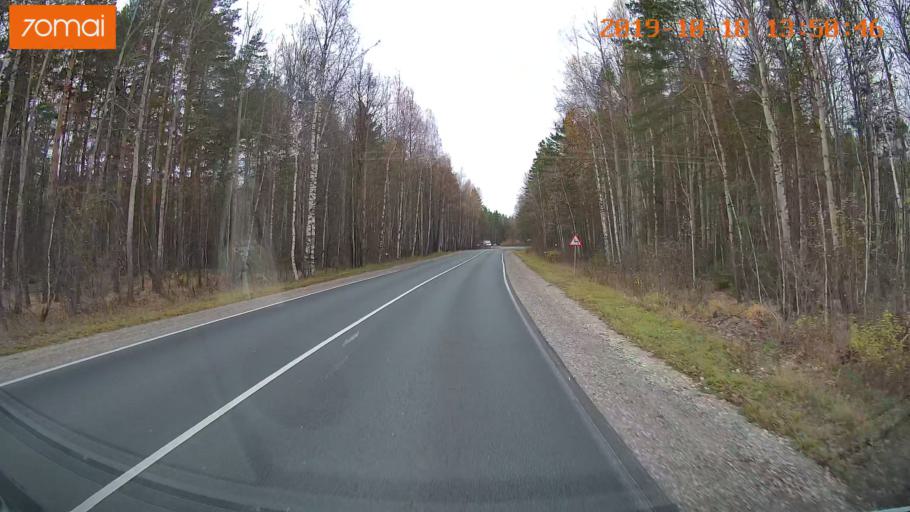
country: RU
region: Moskovskaya
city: Radovitskiy
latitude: 55.0101
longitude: 39.9670
